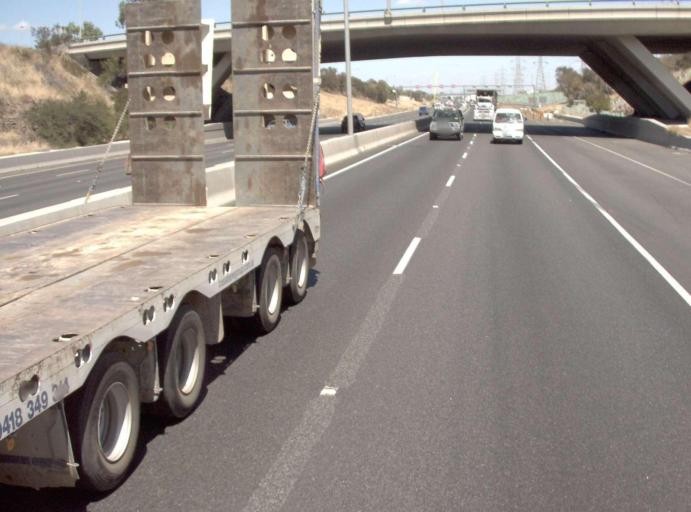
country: AU
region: Victoria
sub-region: Brimbank
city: Kealba
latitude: -37.7502
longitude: 144.8328
